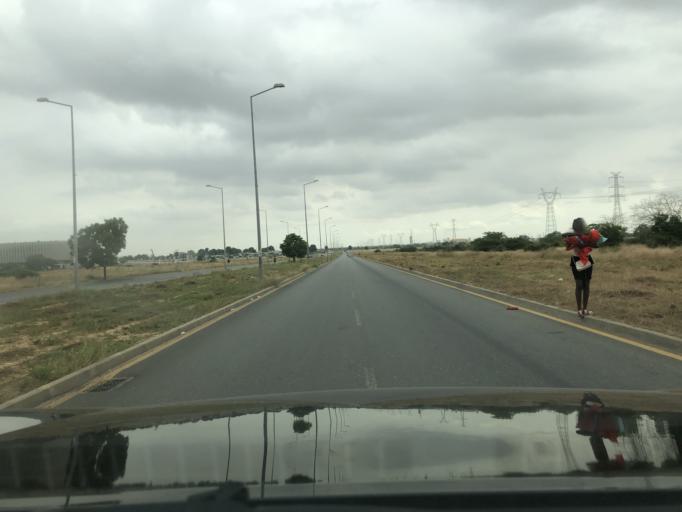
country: AO
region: Luanda
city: Luanda
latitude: -8.9758
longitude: 13.2873
